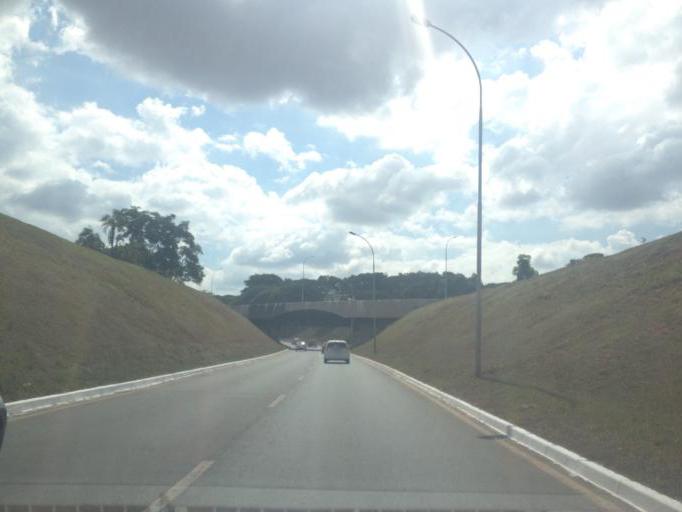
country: BR
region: Federal District
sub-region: Brasilia
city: Brasilia
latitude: -15.8339
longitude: -47.9276
